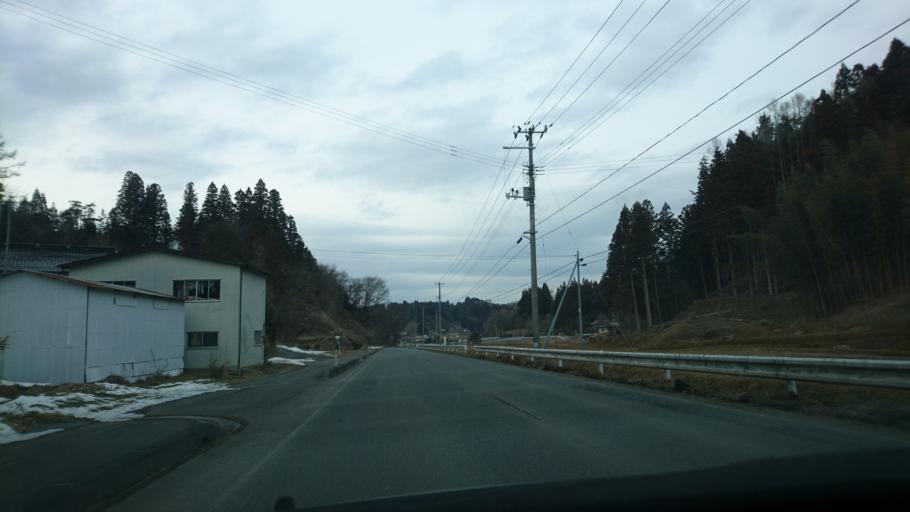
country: JP
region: Iwate
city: Ichinoseki
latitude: 38.9498
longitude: 141.3624
